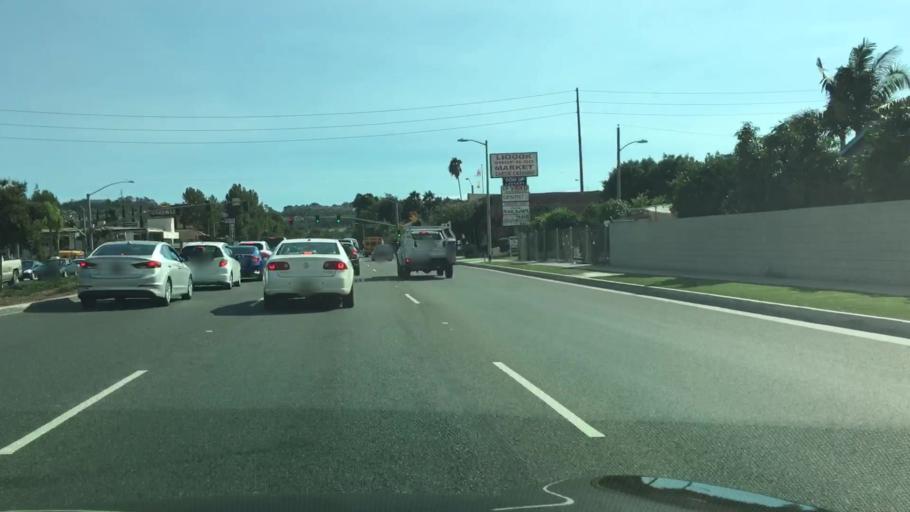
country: US
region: California
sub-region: Los Angeles County
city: East La Mirada
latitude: 33.9258
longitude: -117.9679
